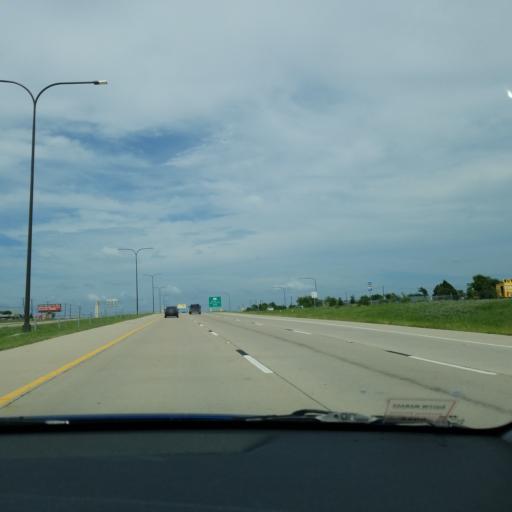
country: US
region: Texas
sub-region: Travis County
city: Manor
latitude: 30.3301
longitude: -97.6310
